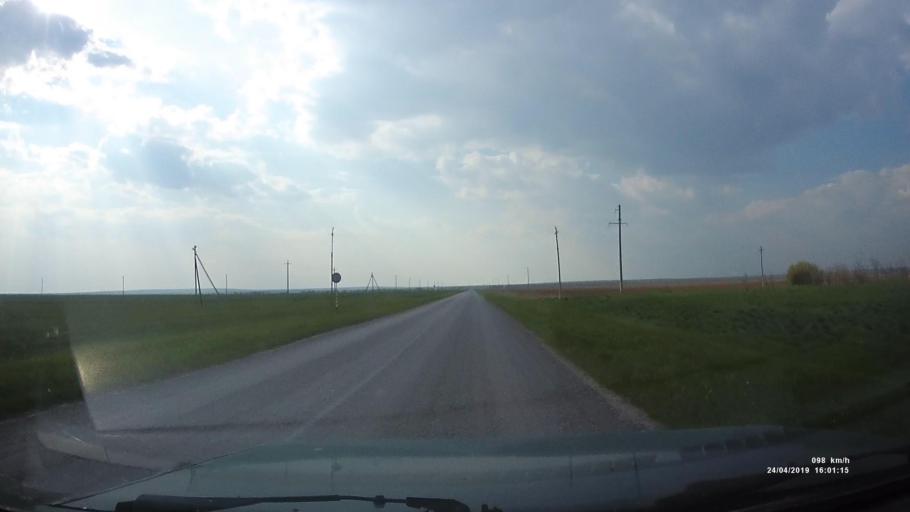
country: RU
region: Rostov
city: Sovetskoye
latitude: 46.6401
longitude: 42.4392
